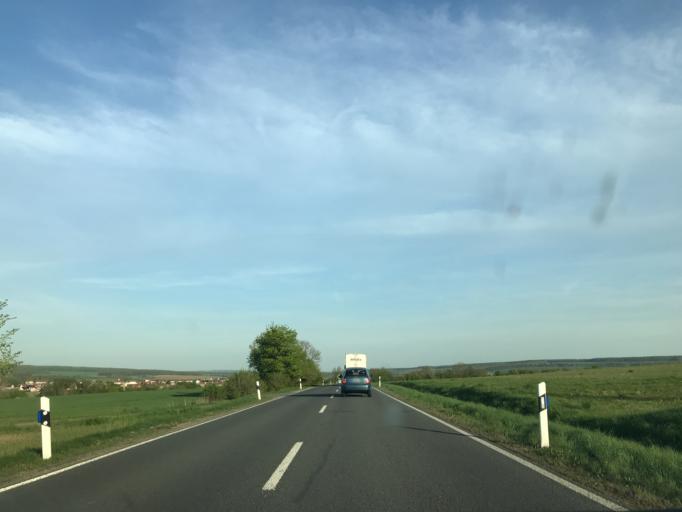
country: DE
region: Thuringia
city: Kefferhausen
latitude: 51.3261
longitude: 10.2976
